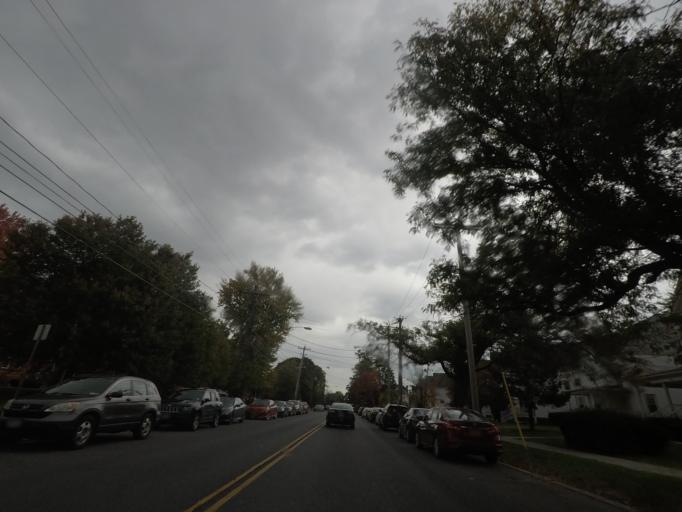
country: US
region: New York
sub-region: Albany County
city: West Albany
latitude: 42.6642
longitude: -73.7846
